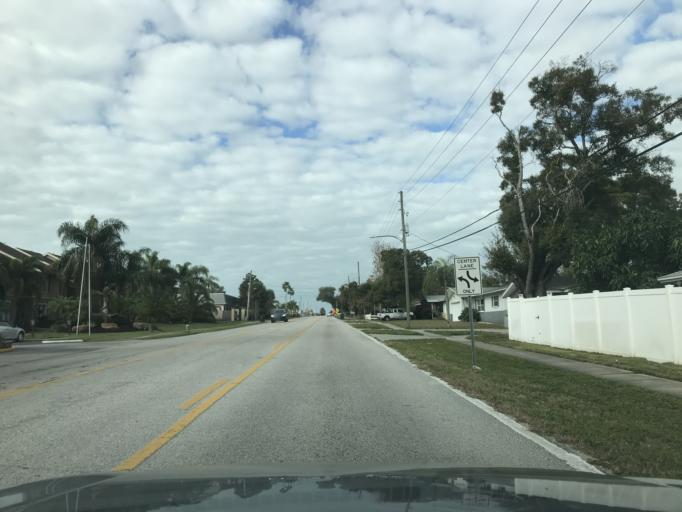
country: US
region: Florida
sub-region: Pinellas County
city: Largo
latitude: 27.9278
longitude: -82.7802
